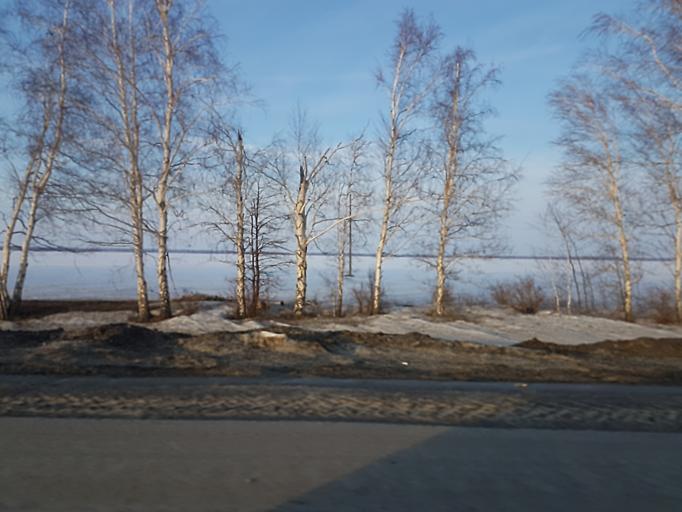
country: RU
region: Tambov
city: Selezni
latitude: 52.8230
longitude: 40.9194
